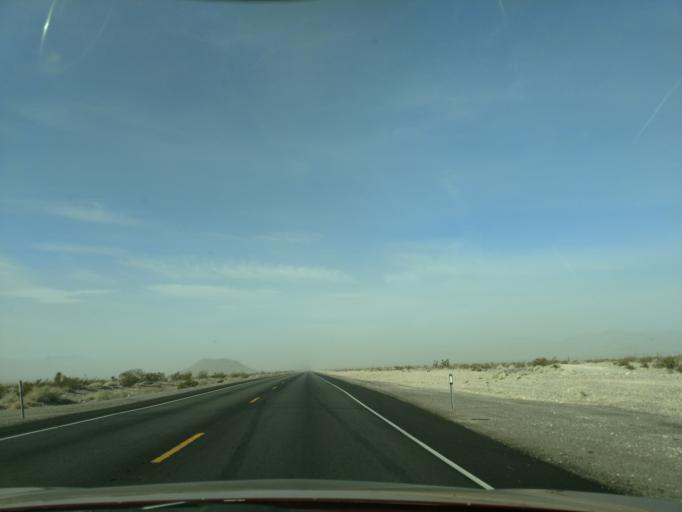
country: US
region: Nevada
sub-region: Nye County
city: Pahrump
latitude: 36.5664
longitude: -116.1339
